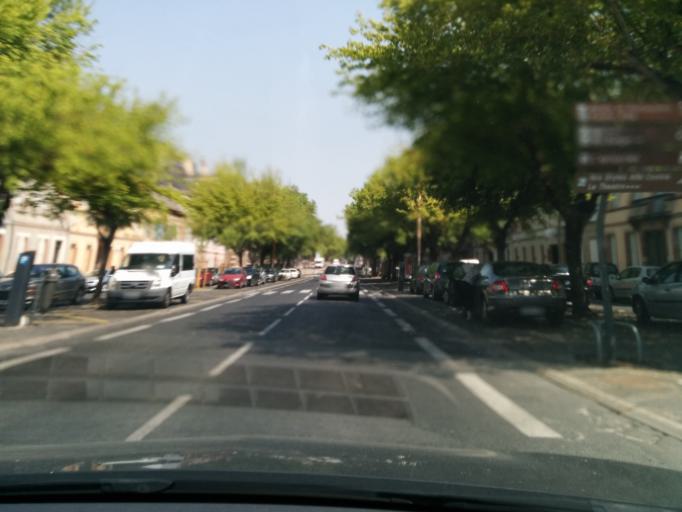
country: FR
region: Midi-Pyrenees
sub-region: Departement du Tarn
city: Albi
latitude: 43.9235
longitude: 2.1490
